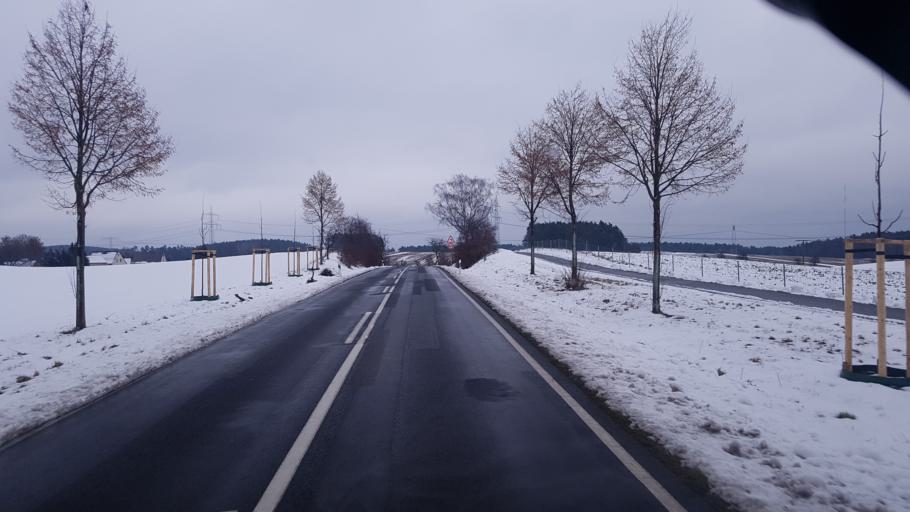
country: DE
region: Brandenburg
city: Lawitz
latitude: 52.0899
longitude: 14.5615
